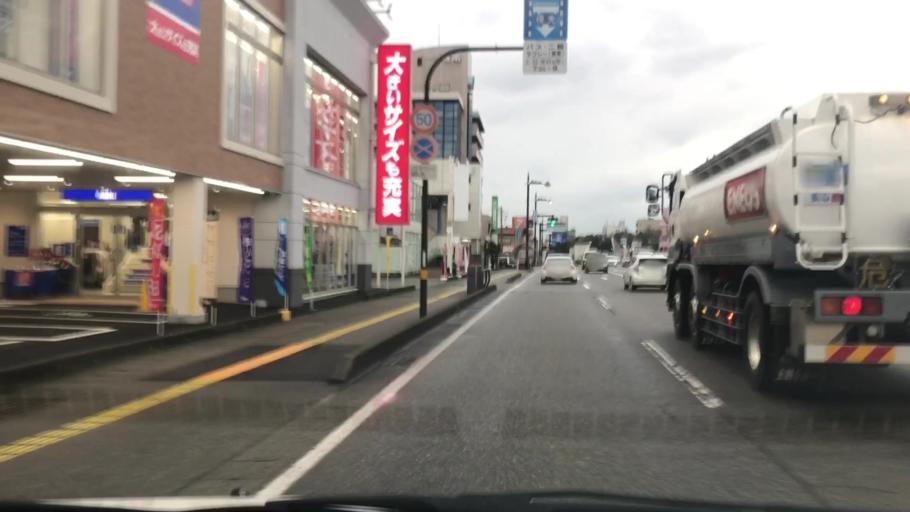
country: JP
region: Toyama
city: Toyama-shi
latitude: 36.6758
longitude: 137.2108
